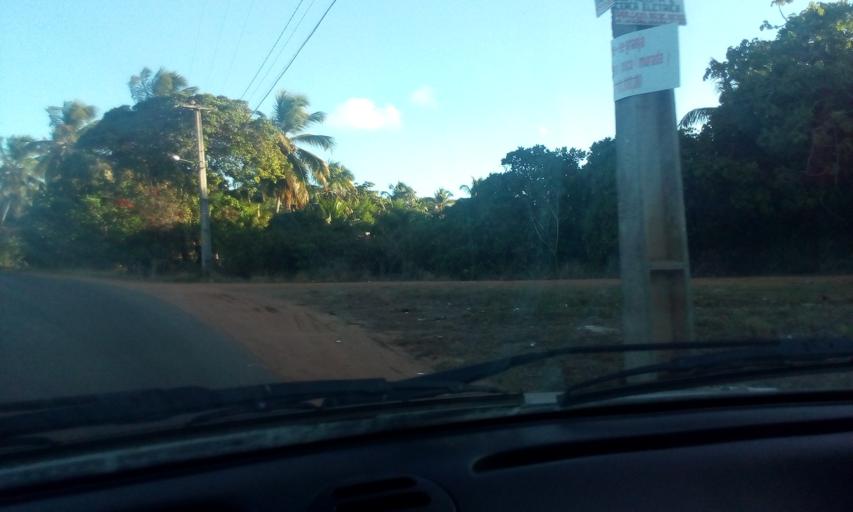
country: BR
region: Rio Grande do Norte
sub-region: Parnamirim
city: Parnamirim
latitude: -5.9578
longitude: -35.1682
